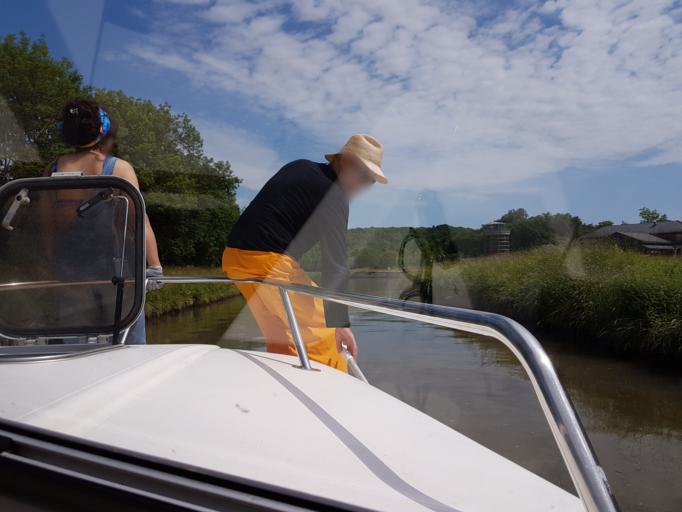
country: FR
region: Bourgogne
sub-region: Departement de la Nievre
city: Clamecy
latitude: 47.4535
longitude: 3.5387
